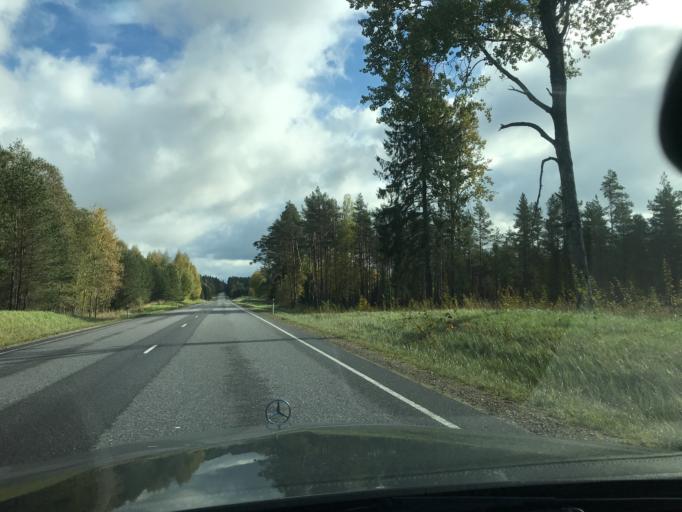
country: EE
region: Vorumaa
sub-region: Voru linn
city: Voru
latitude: 57.7683
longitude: 27.1663
